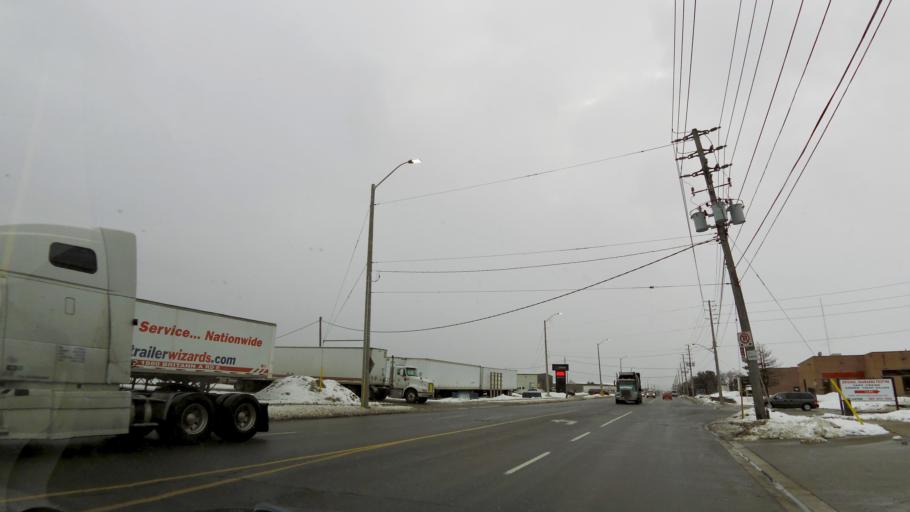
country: CA
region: Ontario
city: Etobicoke
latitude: 43.6620
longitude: -79.6402
